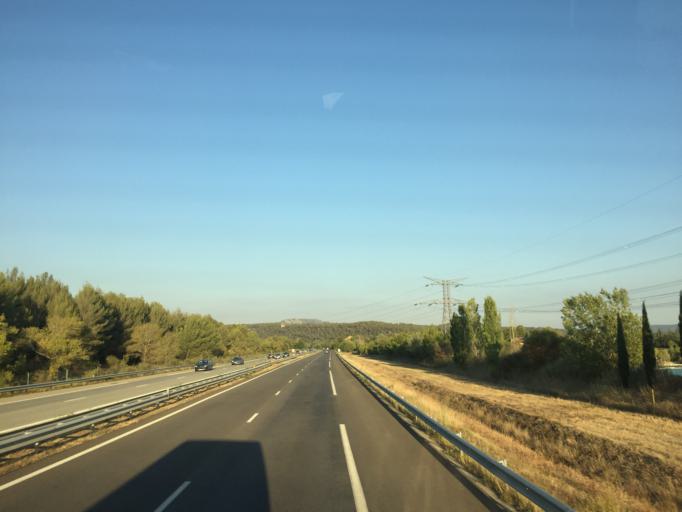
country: FR
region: Provence-Alpes-Cote d'Azur
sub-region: Departement des Bouches-du-Rhone
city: Peyrolles-en-Provence
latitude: 43.6576
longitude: 5.5916
